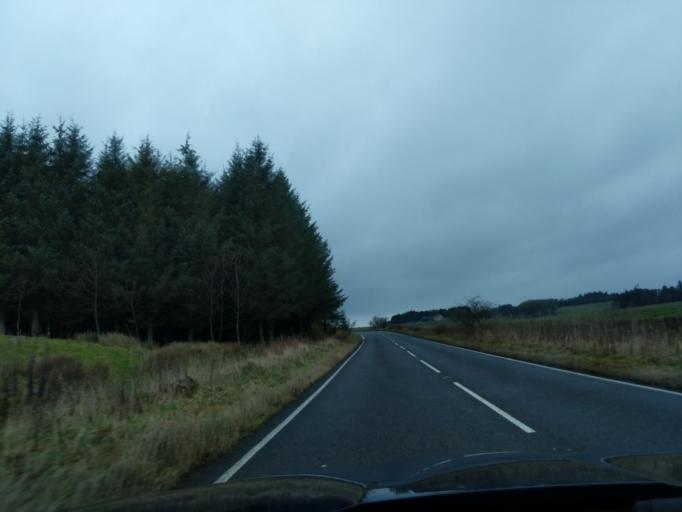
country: GB
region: England
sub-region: Northumberland
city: Corsenside
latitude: 55.1911
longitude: -2.0581
